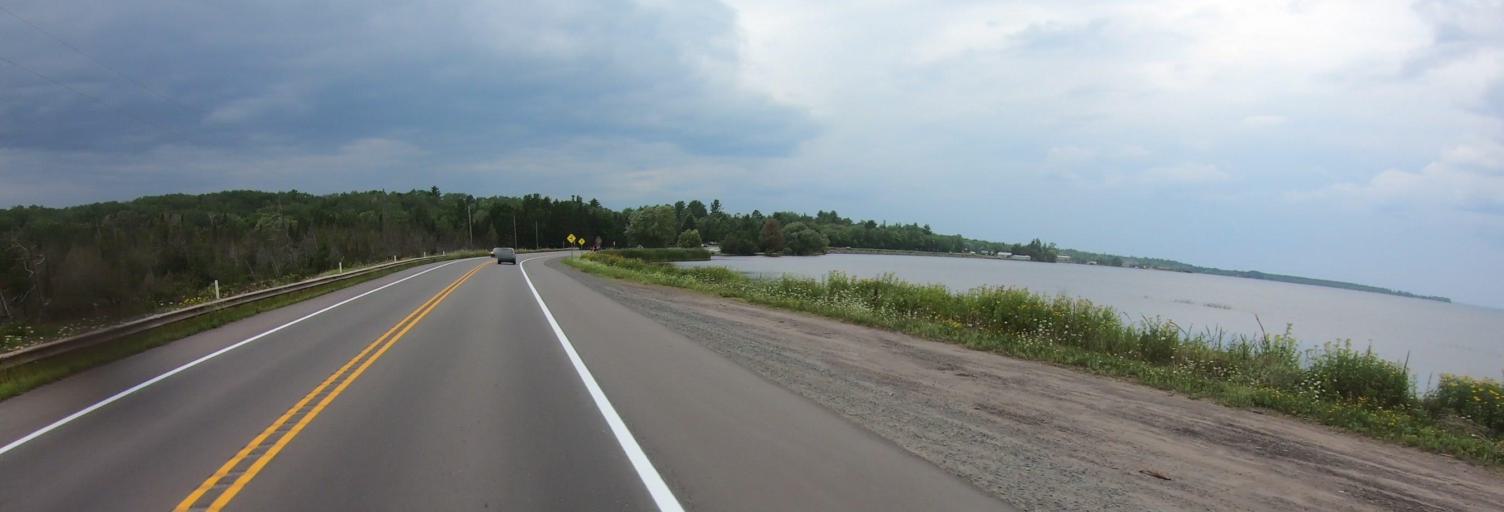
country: US
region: Michigan
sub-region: Baraga County
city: Baraga
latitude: 46.7568
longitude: -88.4992
